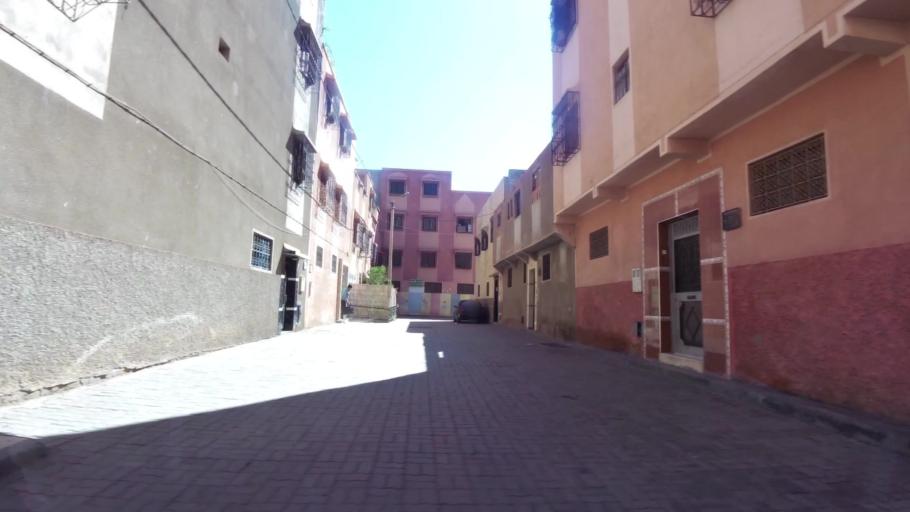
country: MA
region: Marrakech-Tensift-Al Haouz
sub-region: Marrakech
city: Marrakesh
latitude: 31.5904
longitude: -8.0469
